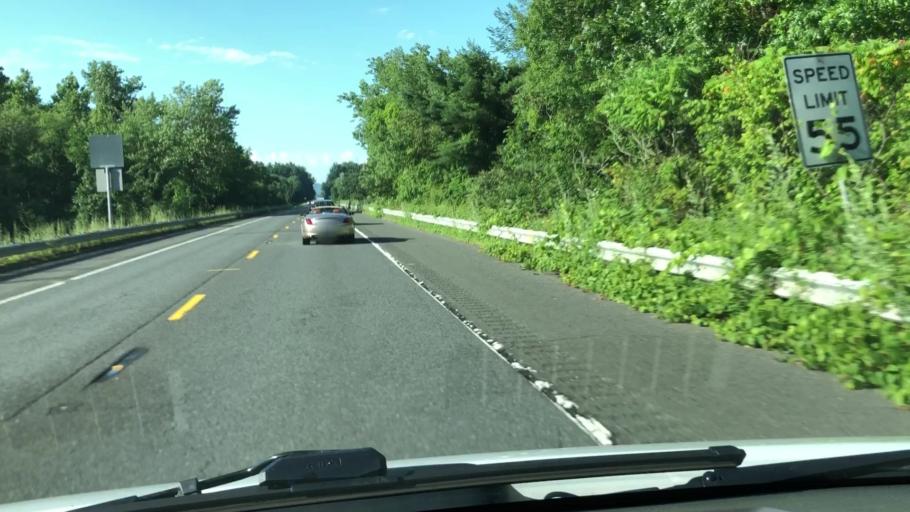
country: US
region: Massachusetts
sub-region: Hampshire County
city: North Amherst
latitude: 42.4068
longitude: -72.5382
